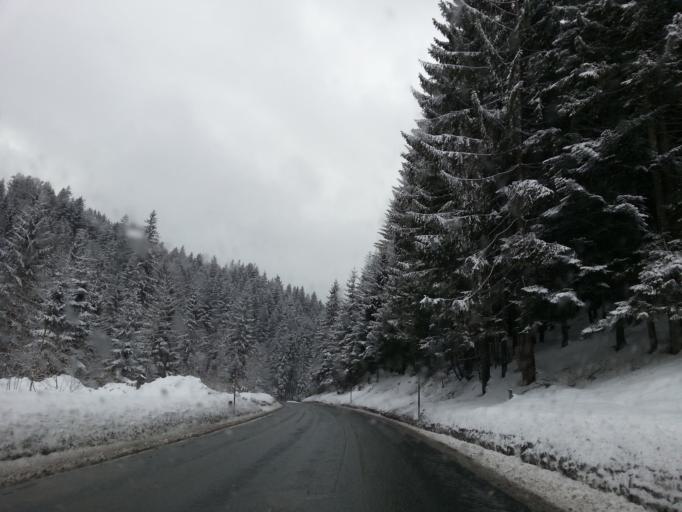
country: AT
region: Salzburg
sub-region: Politischer Bezirk Sankt Johann im Pongau
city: Eben im Pongau
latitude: 47.4809
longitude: 13.3920
